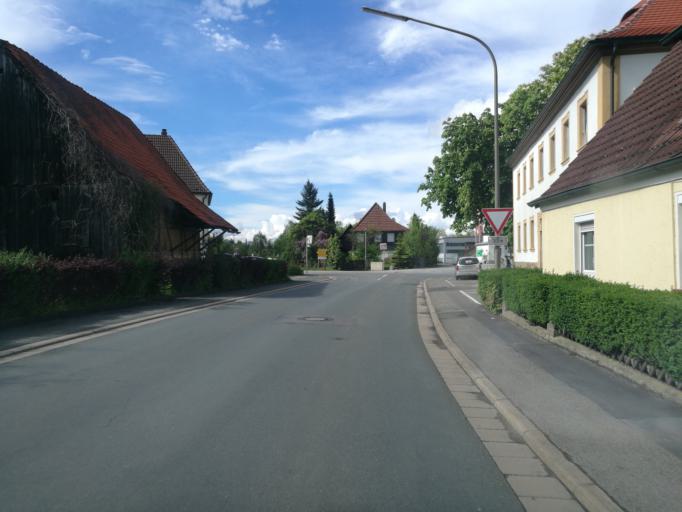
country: DE
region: Bavaria
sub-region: Upper Franconia
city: Weismain
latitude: 50.0860
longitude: 11.2448
